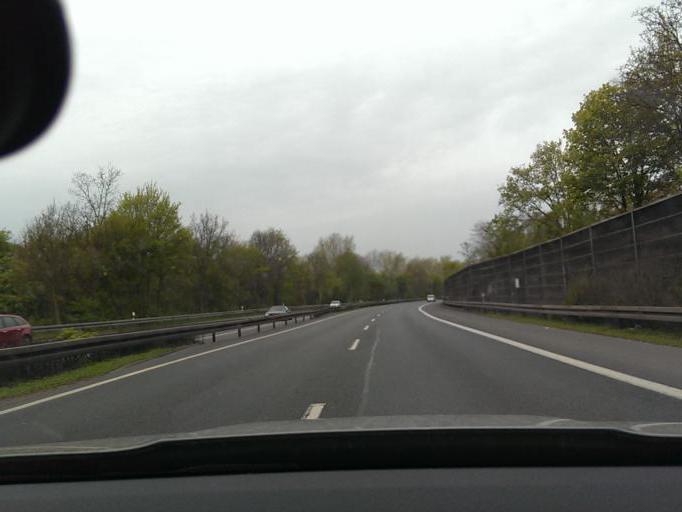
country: DE
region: Lower Saxony
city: Hannover
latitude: 52.3911
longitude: 9.6827
